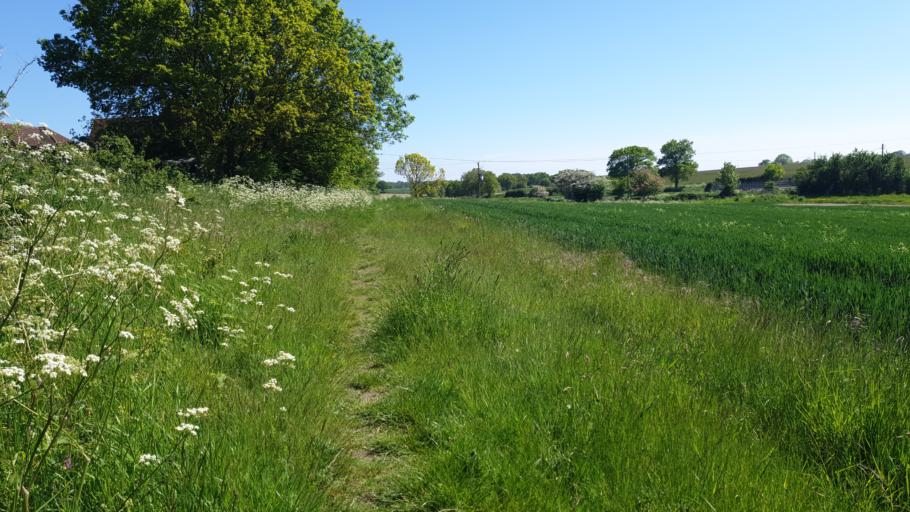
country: GB
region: England
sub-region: Essex
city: Great Bentley
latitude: 51.8559
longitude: 1.0533
